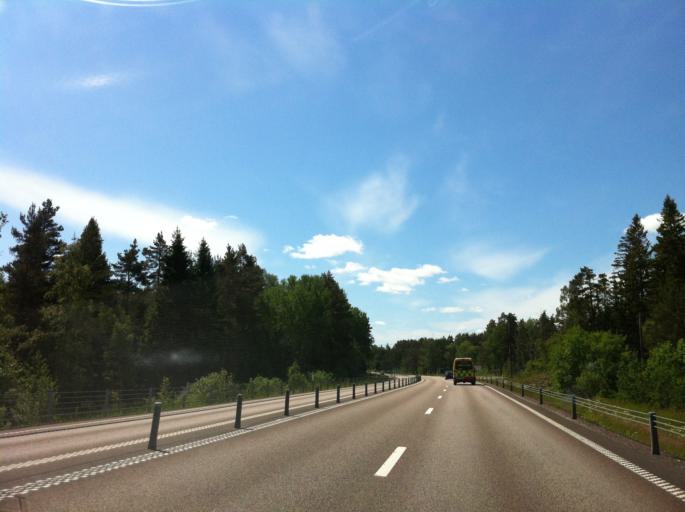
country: SE
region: Vaestra Goetaland
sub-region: Melleruds Kommun
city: Mellerud
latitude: 58.8270
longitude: 12.5276
